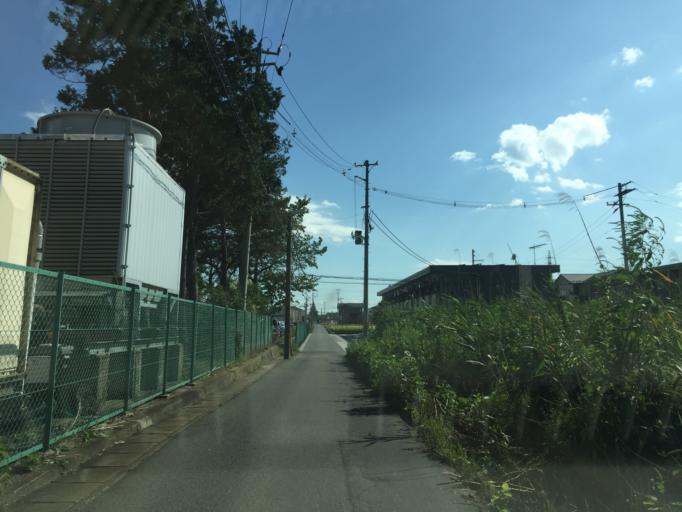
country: JP
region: Fukushima
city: Koriyama
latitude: 37.4117
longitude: 140.4009
